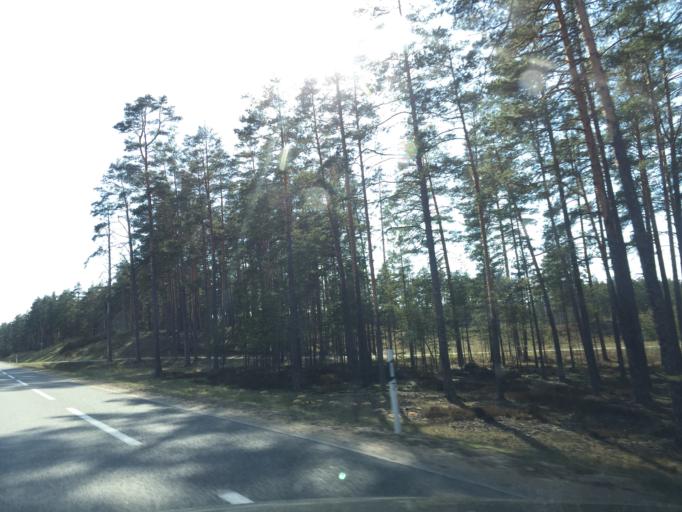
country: LV
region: Saulkrastu
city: Saulkrasti
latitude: 57.2134
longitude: 24.3959
